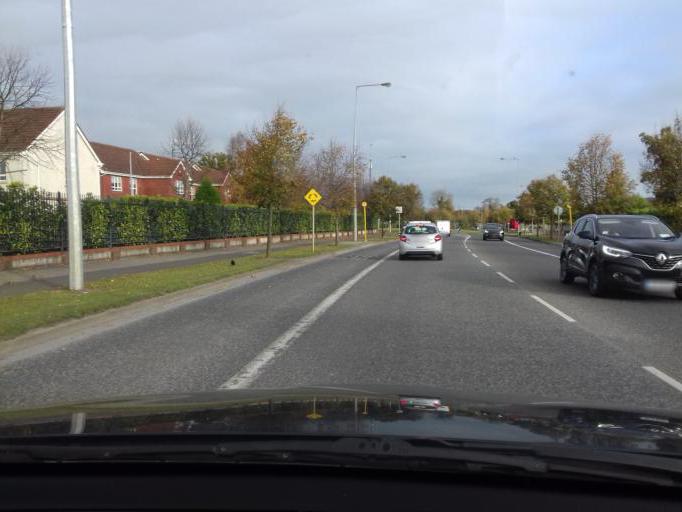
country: IE
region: Leinster
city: Hartstown
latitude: 53.3975
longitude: -6.4424
